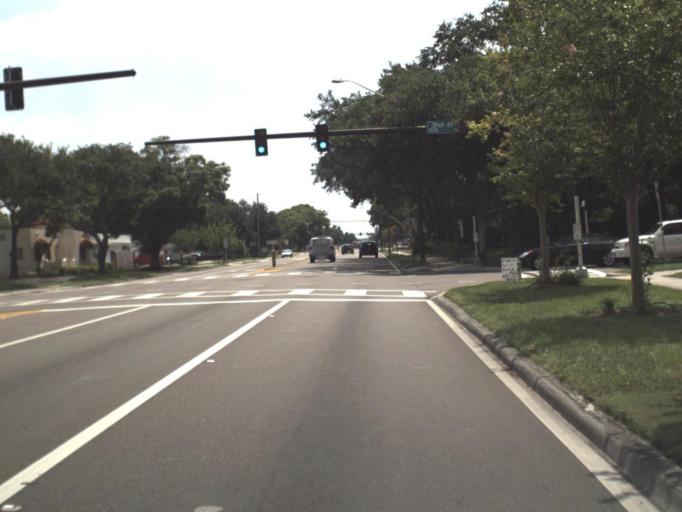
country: US
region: Florida
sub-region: Pinellas County
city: Saint Petersburg
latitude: 27.7773
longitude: -82.6758
